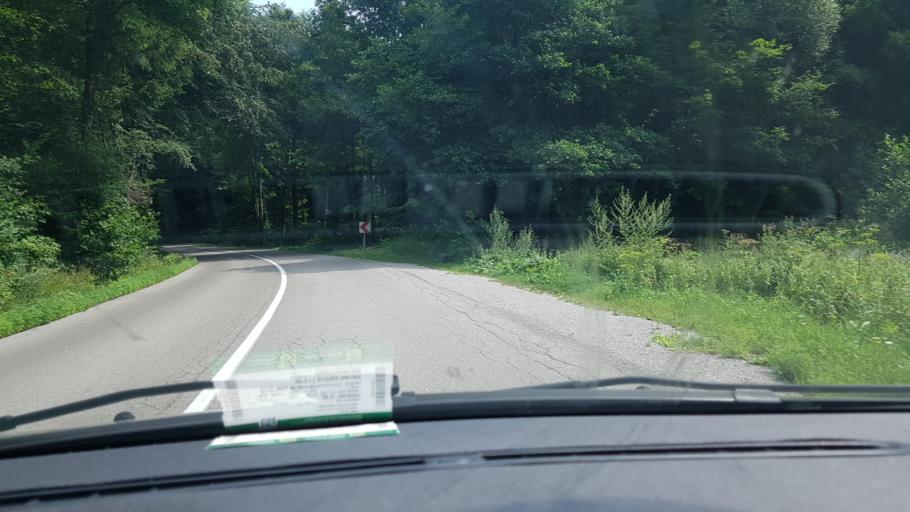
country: HR
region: Primorsko-Goranska
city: Hreljin
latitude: 45.3311
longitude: 14.6812
